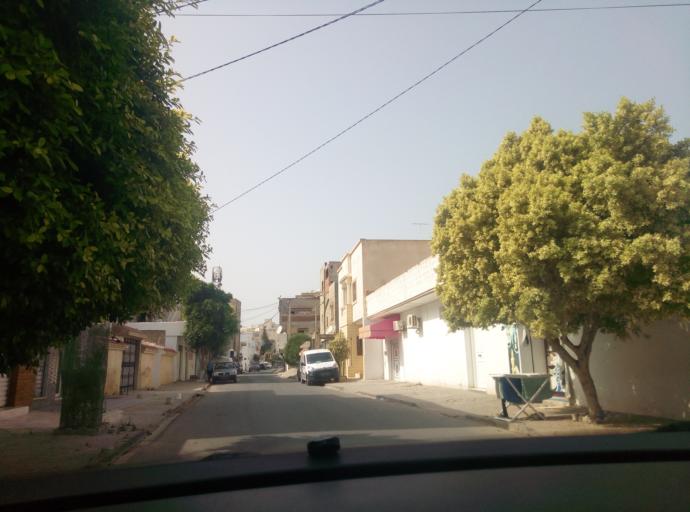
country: TN
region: Tunis
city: La Goulette
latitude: 36.8538
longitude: 10.2710
